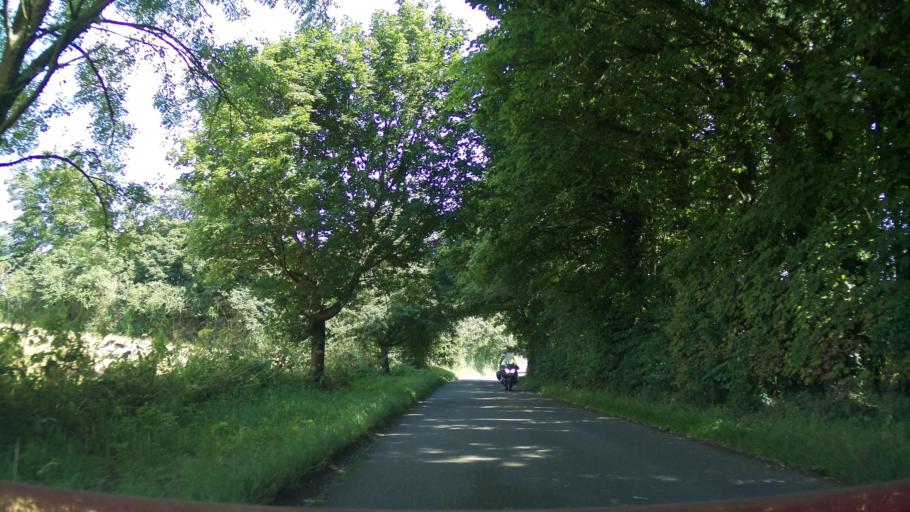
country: GB
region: England
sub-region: West Berkshire
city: Farnborough
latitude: 51.5106
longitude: -1.3926
